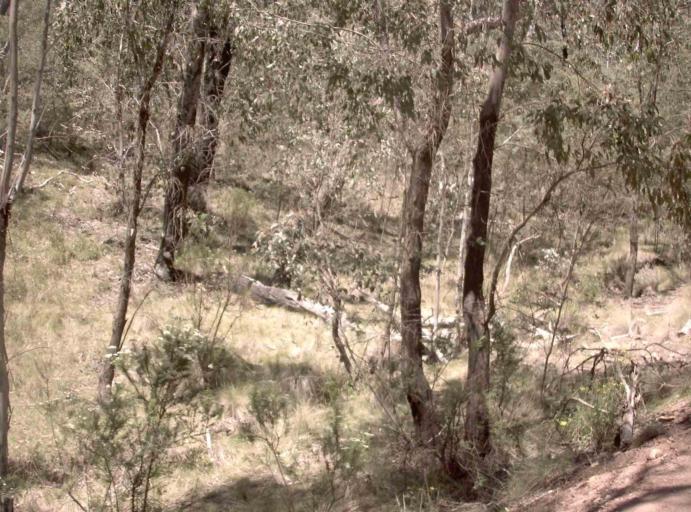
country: AU
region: New South Wales
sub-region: Snowy River
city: Jindabyne
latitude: -37.0614
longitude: 148.3168
